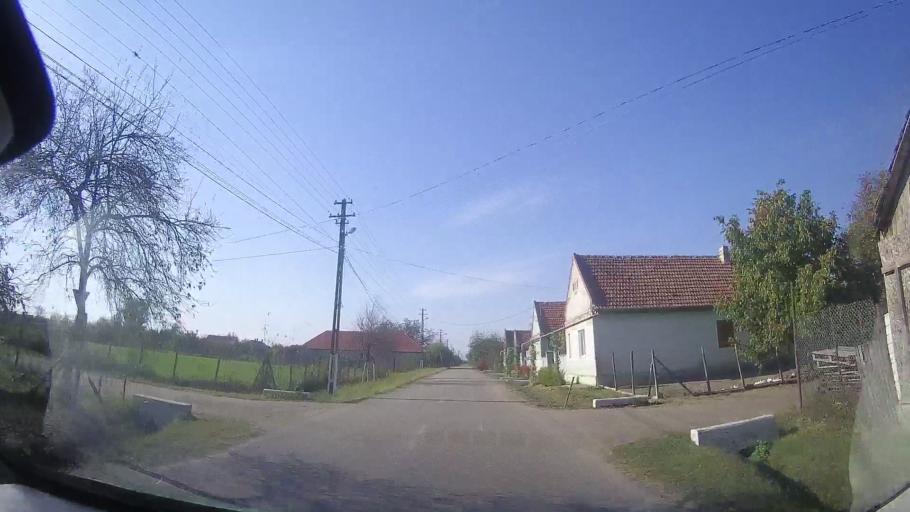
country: RO
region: Timis
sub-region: Comuna Topolovatu Mare
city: Topolovatu Mare
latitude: 45.7926
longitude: 21.5862
